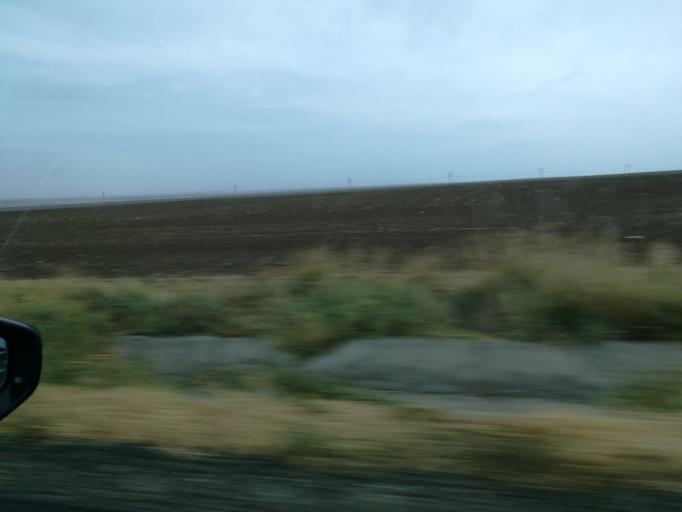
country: RO
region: Constanta
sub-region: Comuna Cogealac
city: Cogealac
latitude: 44.5447
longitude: 28.5861
